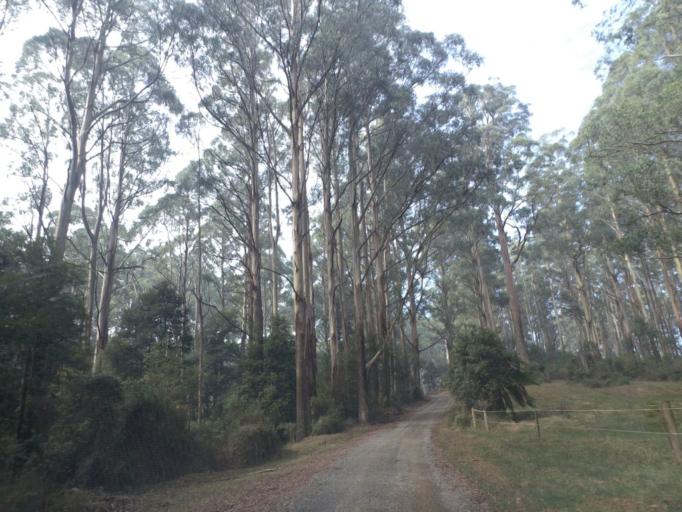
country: AU
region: Victoria
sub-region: Yarra Ranges
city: Healesville
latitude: -37.5589
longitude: 145.5347
